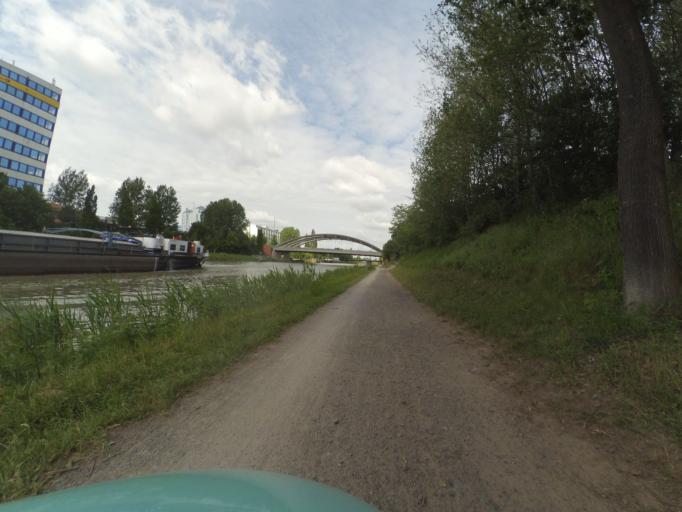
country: DE
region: Lower Saxony
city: Hannover
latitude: 52.4073
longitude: 9.7419
